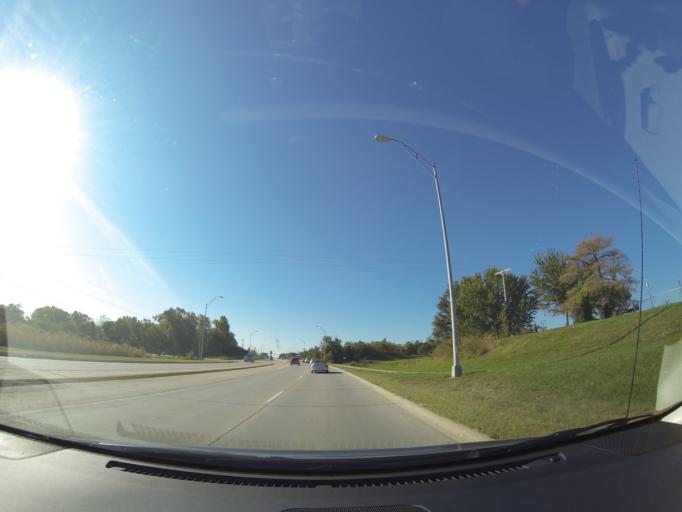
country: US
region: Nebraska
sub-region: Sarpy County
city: Gretna
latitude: 41.1508
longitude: -96.2389
